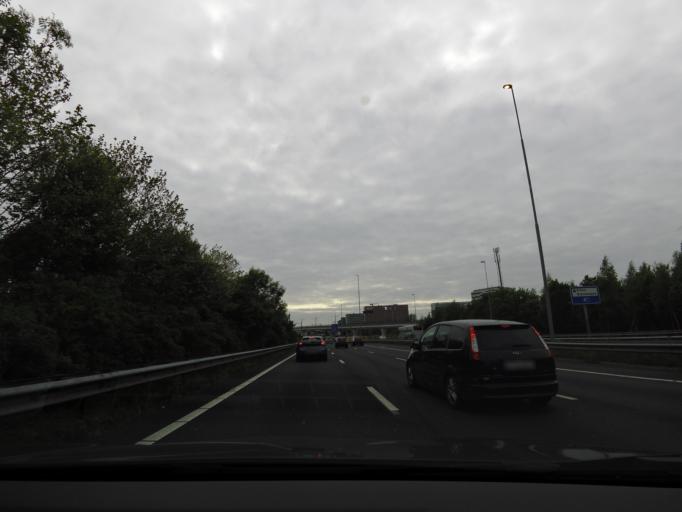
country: NL
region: North Holland
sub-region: Gemeente Amstelveen
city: Amstelveen
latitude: 52.3389
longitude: 4.8356
